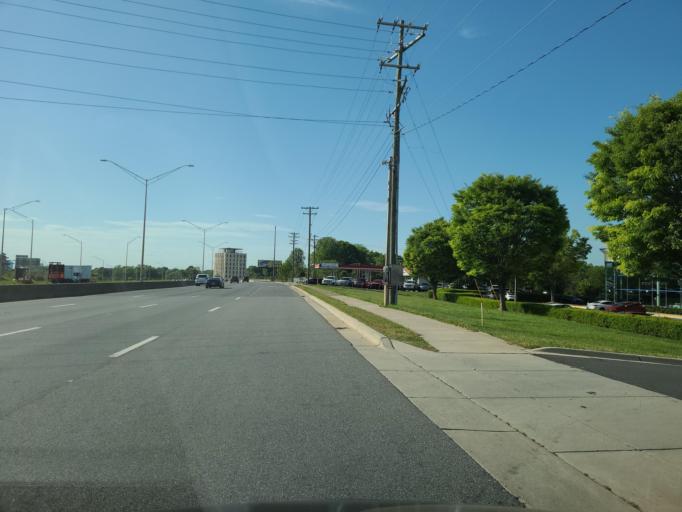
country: US
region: North Carolina
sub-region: Mecklenburg County
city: Charlotte
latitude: 35.1973
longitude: -80.7684
